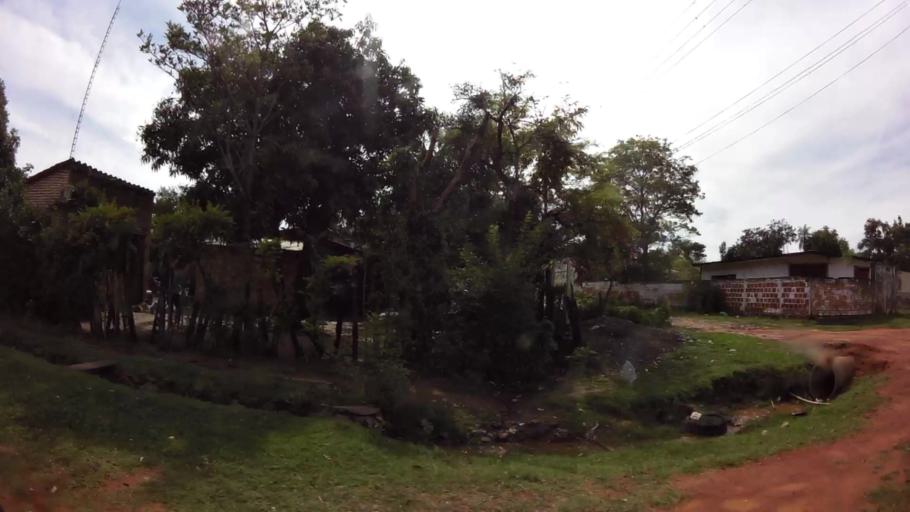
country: PY
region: Presidente Hayes
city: Villa Hayes
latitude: -25.1076
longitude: -57.4890
